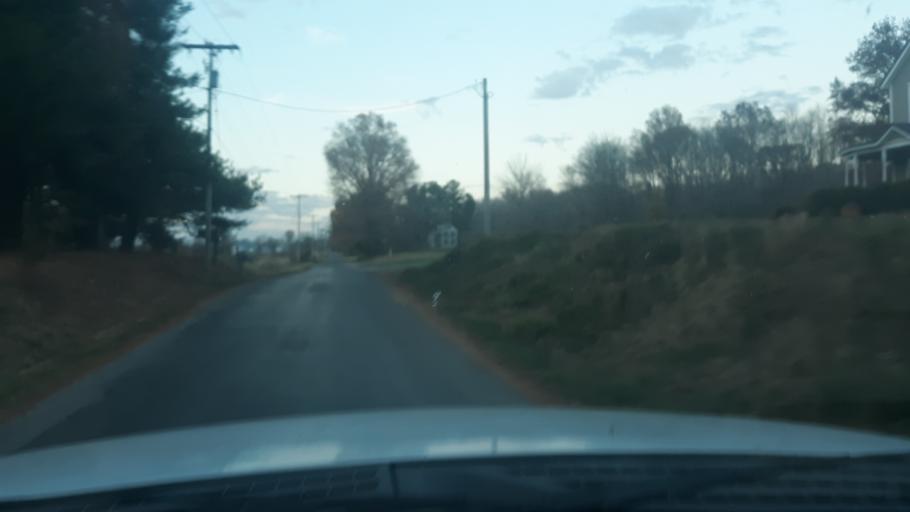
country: US
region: Illinois
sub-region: Saline County
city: Harrisburg
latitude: 37.8432
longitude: -88.6145
